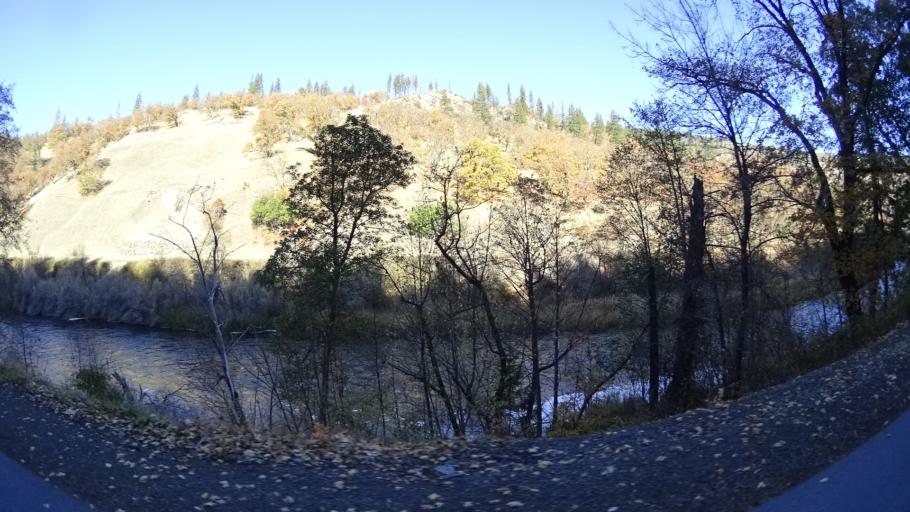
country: US
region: California
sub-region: Siskiyou County
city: Yreka
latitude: 41.8425
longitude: -122.9116
